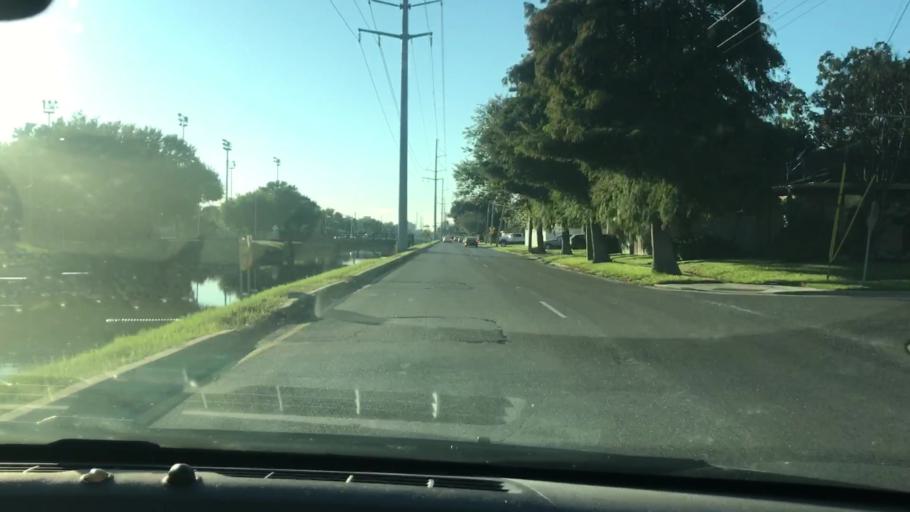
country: US
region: Louisiana
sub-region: Jefferson Parish
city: Metairie
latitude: 30.0135
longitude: -90.1295
